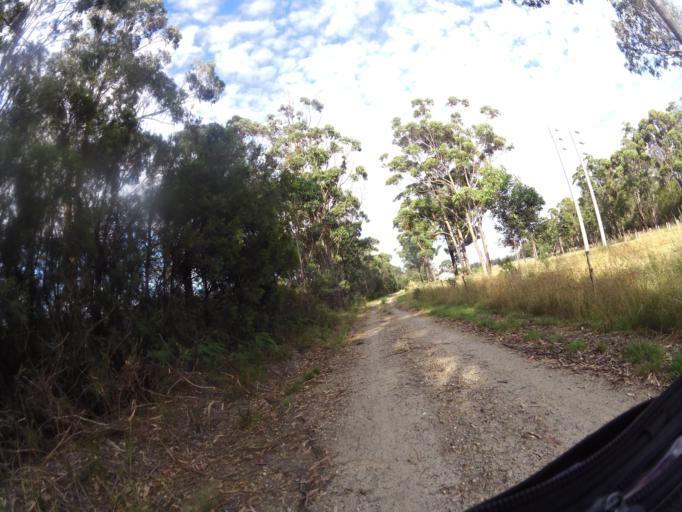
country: AU
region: Victoria
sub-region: East Gippsland
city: Lakes Entrance
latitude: -37.7458
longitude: 148.4089
